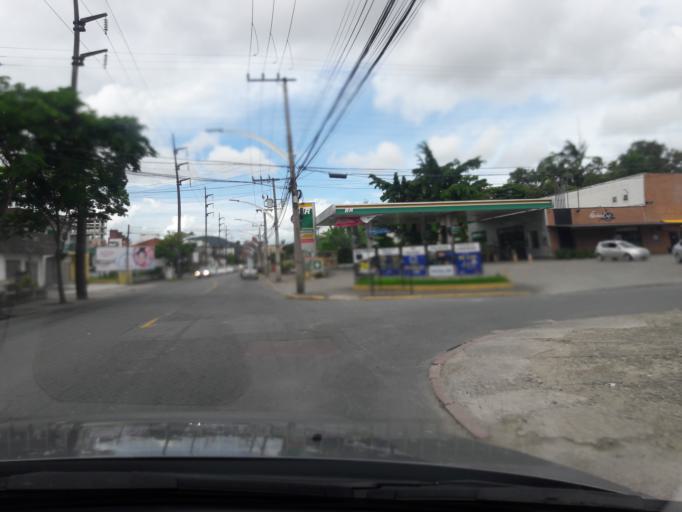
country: BR
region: Santa Catarina
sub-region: Joinville
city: Joinville
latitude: -26.3225
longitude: -48.8535
